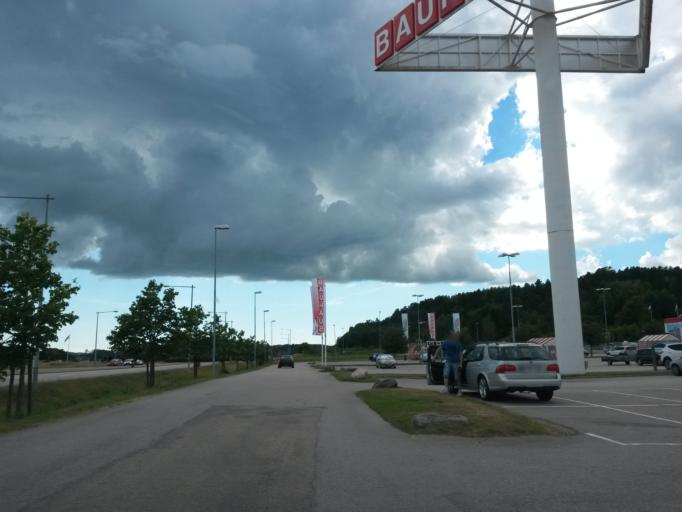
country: SE
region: Vaestra Goetaland
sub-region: Uddevalla Kommun
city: Uddevalla
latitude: 58.3516
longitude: 11.8062
